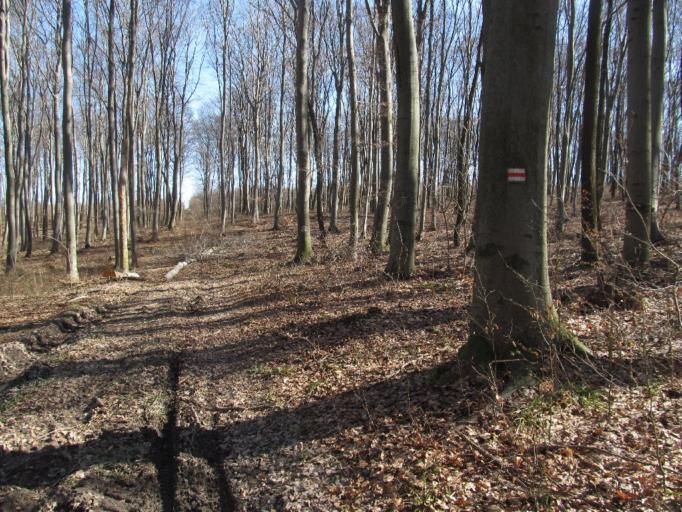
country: HU
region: Fejer
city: Bakonycsernye
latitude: 47.2778
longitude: 18.1053
